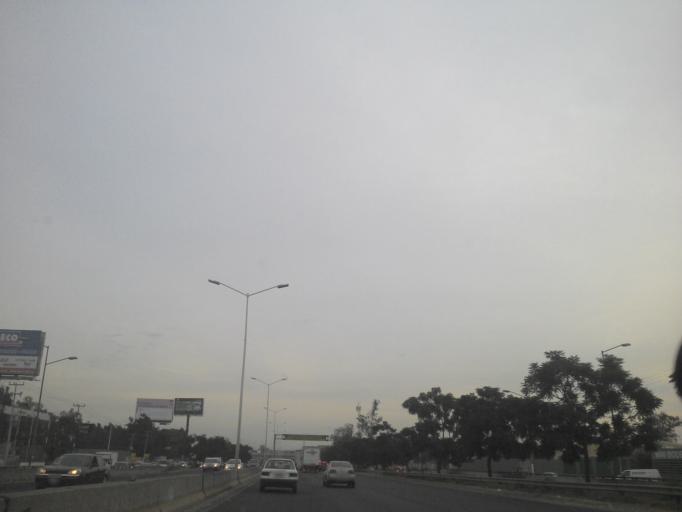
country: MX
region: Jalisco
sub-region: Tlajomulco de Zuniga
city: Palomar
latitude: 20.6348
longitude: -103.4378
